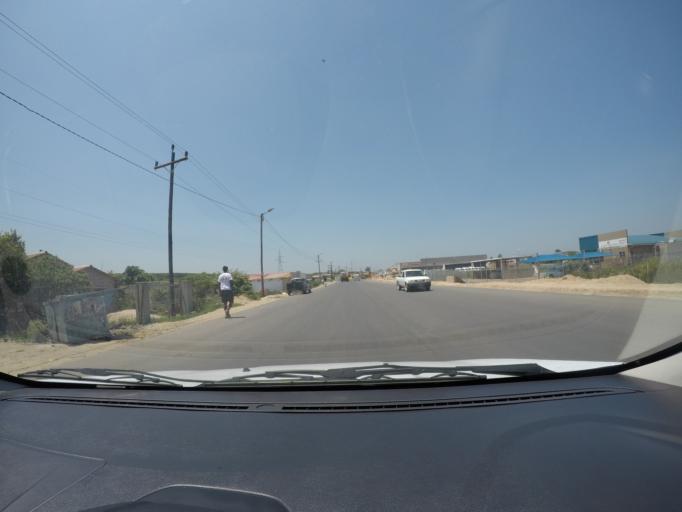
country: ZA
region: KwaZulu-Natal
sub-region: uThungulu District Municipality
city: eSikhawini
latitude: -28.8737
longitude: 31.8973
